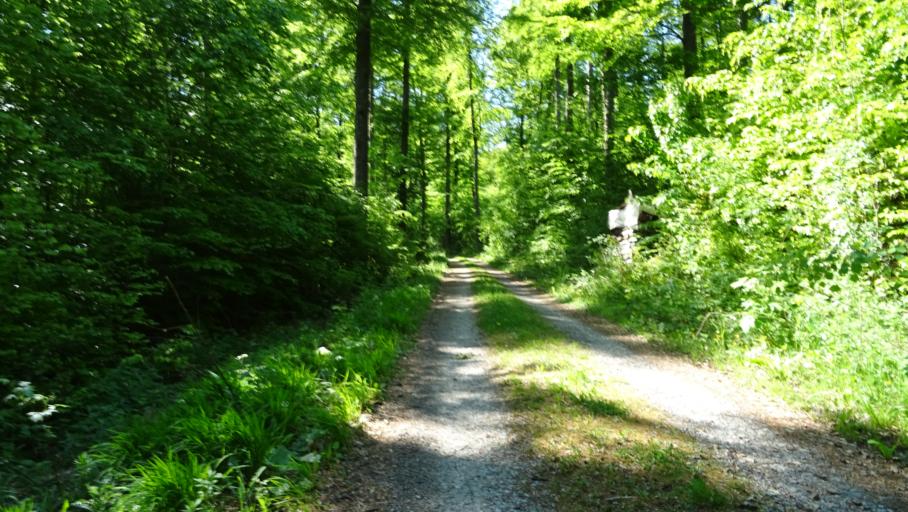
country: DE
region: Baden-Wuerttemberg
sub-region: Karlsruhe Region
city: Limbach
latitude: 49.4104
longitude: 9.2307
